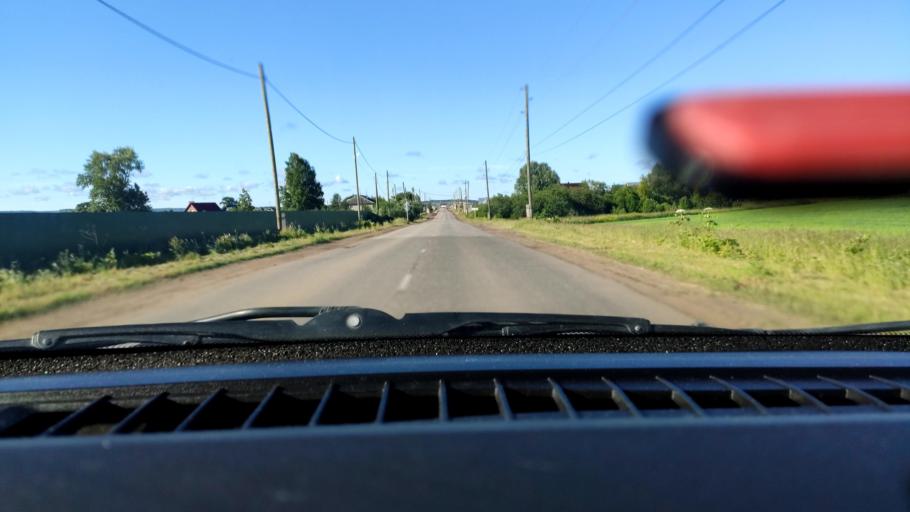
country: RU
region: Perm
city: Kultayevo
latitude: 57.8750
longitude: 55.9197
